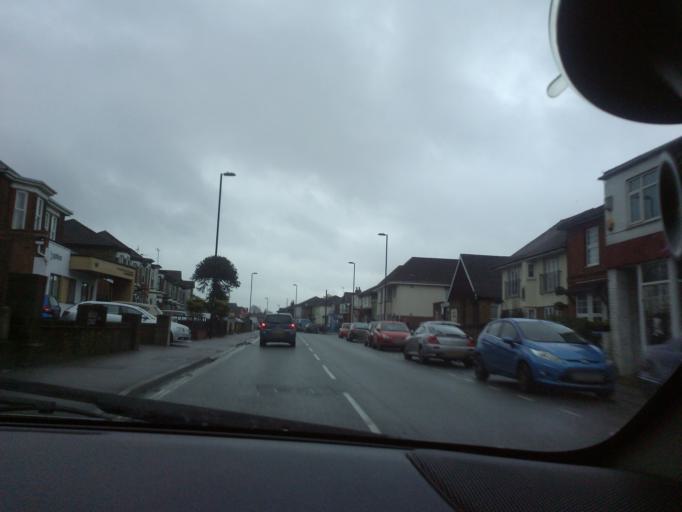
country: GB
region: England
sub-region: Southampton
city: Southampton
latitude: 50.9135
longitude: -1.4222
